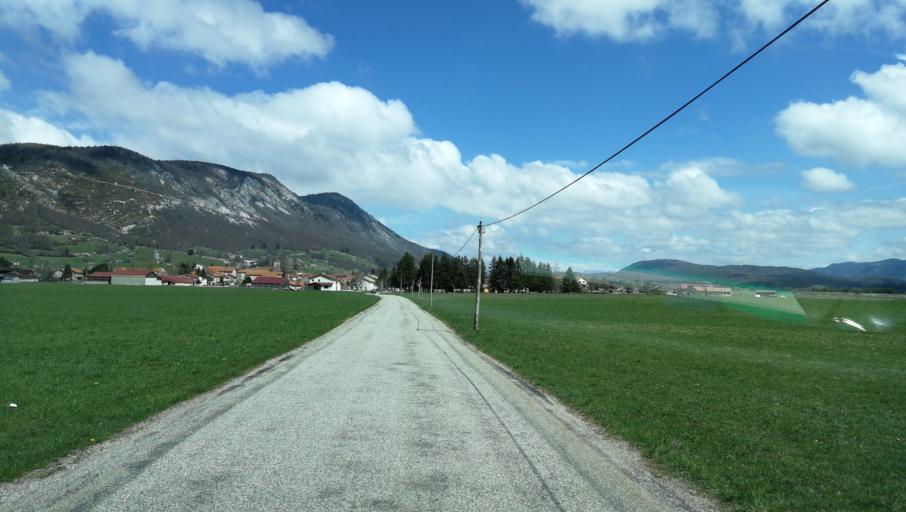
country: FR
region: Rhone-Alpes
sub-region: Departement de la Drome
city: Die
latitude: 44.8892
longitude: 5.3701
